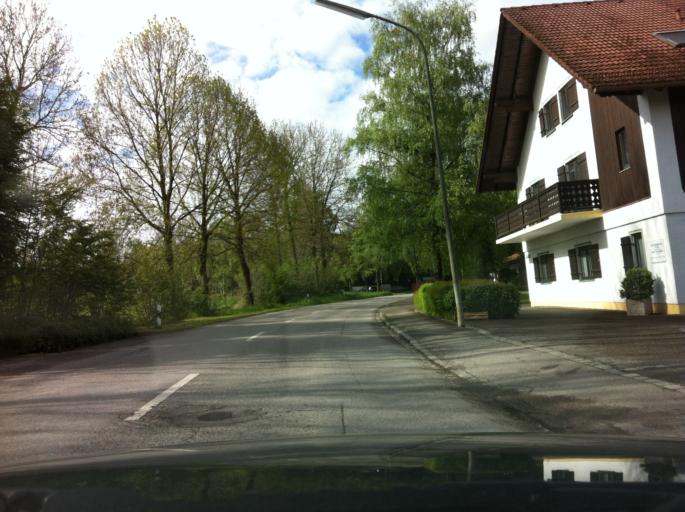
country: DE
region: Bavaria
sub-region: Upper Bavaria
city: Taufkirchen
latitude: 48.0373
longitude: 11.6159
